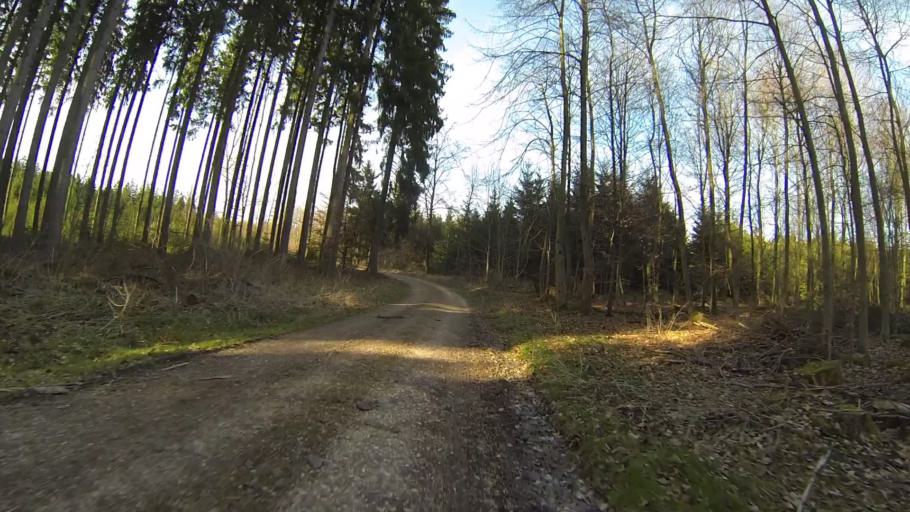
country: DE
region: Baden-Wuerttemberg
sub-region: Regierungsbezirk Stuttgart
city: Niederstotzingen
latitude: 48.5644
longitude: 10.2272
